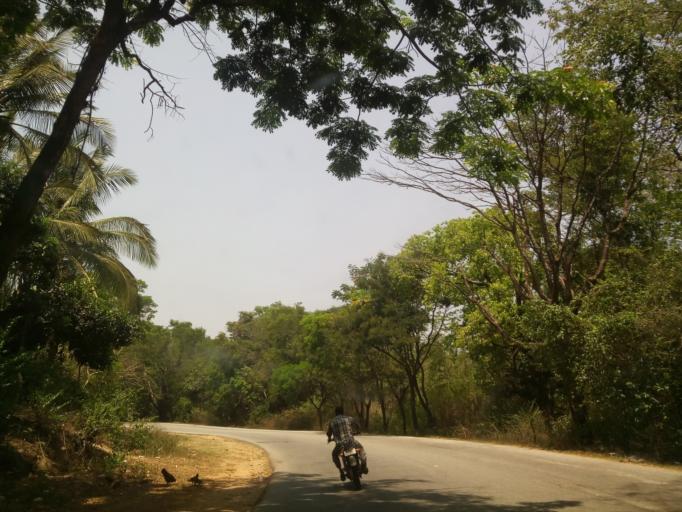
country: IN
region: Karnataka
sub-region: Hassan
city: Sakleshpur
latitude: 12.9547
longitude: 75.8579
